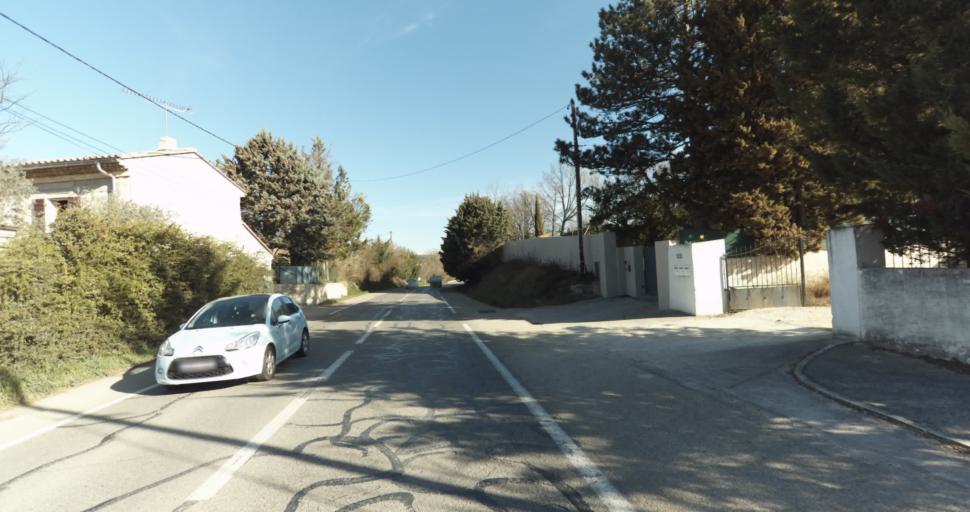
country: FR
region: Provence-Alpes-Cote d'Azur
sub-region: Departement des Bouches-du-Rhone
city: Aix-en-Provence
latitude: 43.5740
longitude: 5.4323
